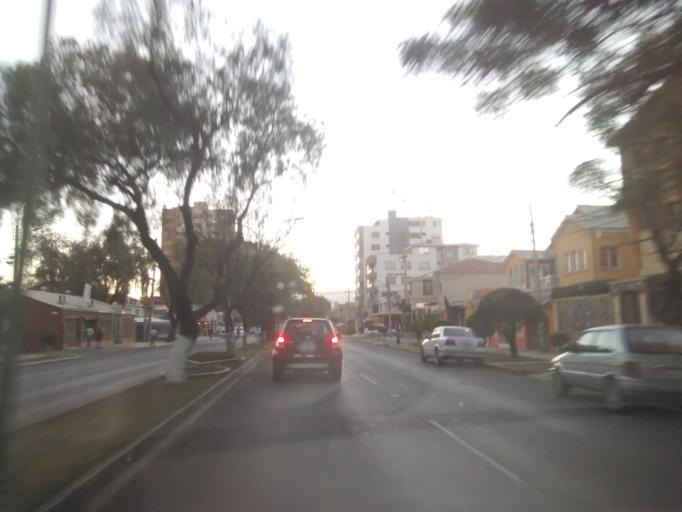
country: BO
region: Cochabamba
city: Cochabamba
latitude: -17.3723
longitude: -66.1652
